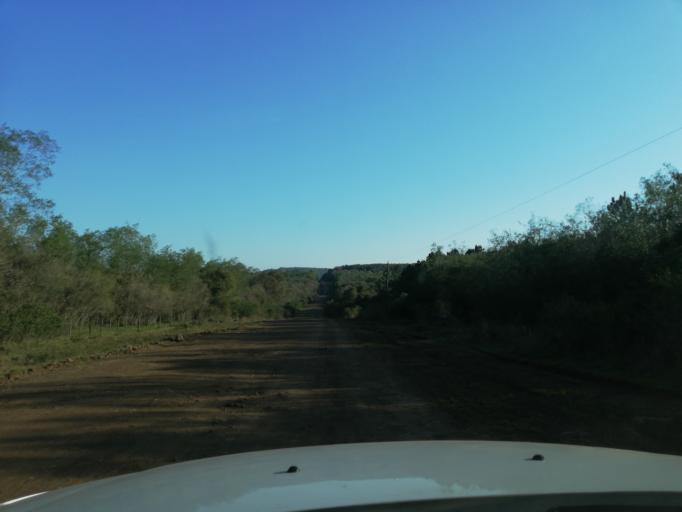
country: AR
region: Misiones
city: Cerro Cora
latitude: -27.5896
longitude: -55.6909
